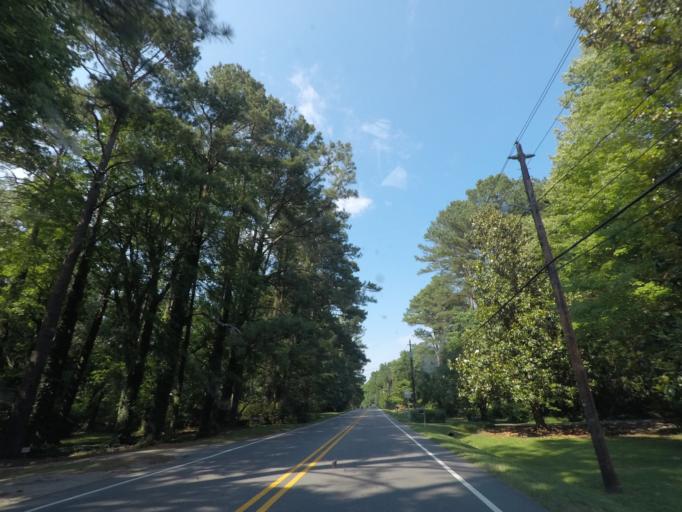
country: US
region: North Carolina
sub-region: Durham County
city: Durham
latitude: 35.9477
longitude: -78.9409
